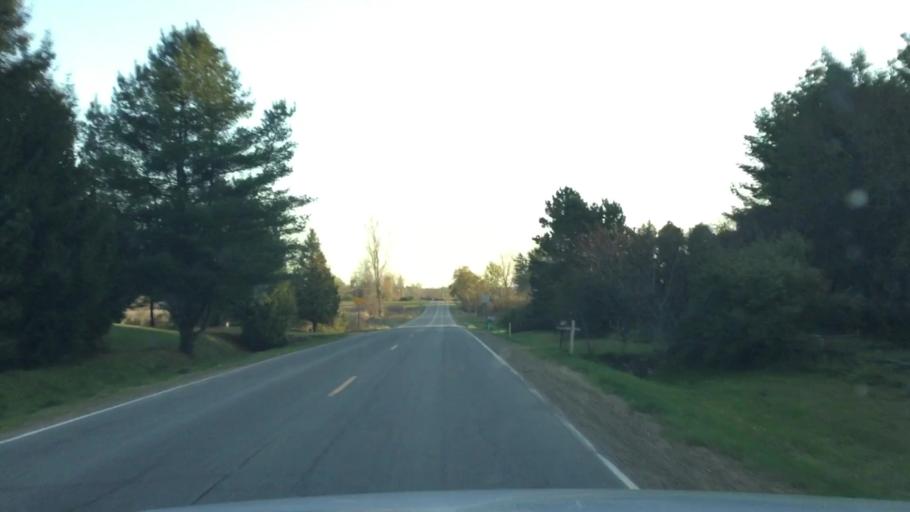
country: US
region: Michigan
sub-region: Sanilac County
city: Marlette
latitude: 43.3338
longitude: -83.1837
